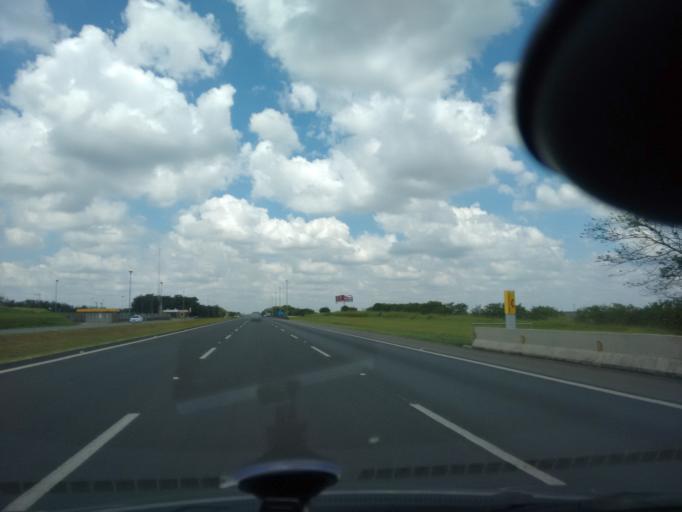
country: BR
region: Sao Paulo
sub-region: Santa Barbara D'Oeste
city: Santa Barbara d'Oeste
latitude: -22.8104
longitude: -47.3903
